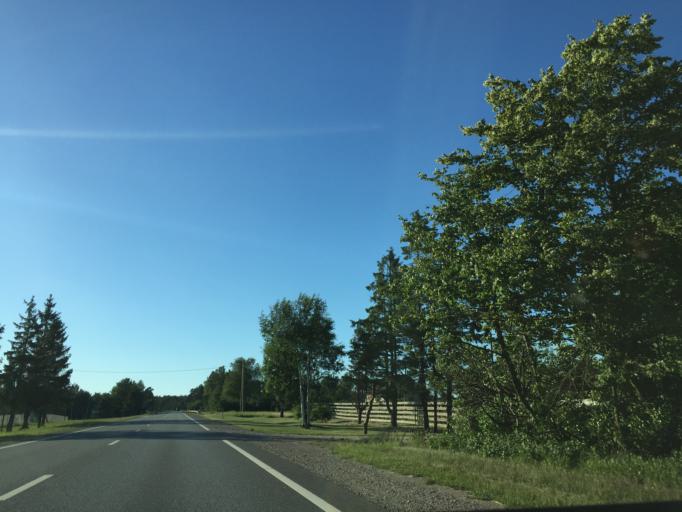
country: LV
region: Ventspils
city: Ventspils
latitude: 57.3936
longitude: 21.6984
